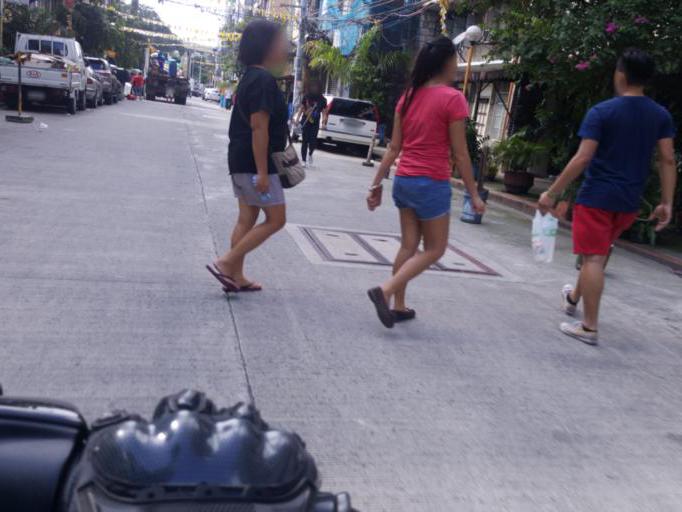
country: PH
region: Metro Manila
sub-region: City of Manila
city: Manila
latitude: 14.6071
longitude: 120.9870
